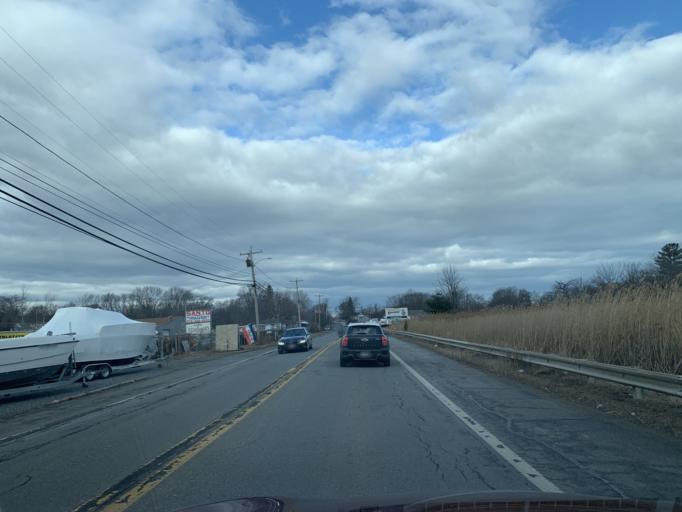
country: US
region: Massachusetts
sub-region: Essex County
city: Salisbury
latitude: 42.8352
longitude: -70.8617
